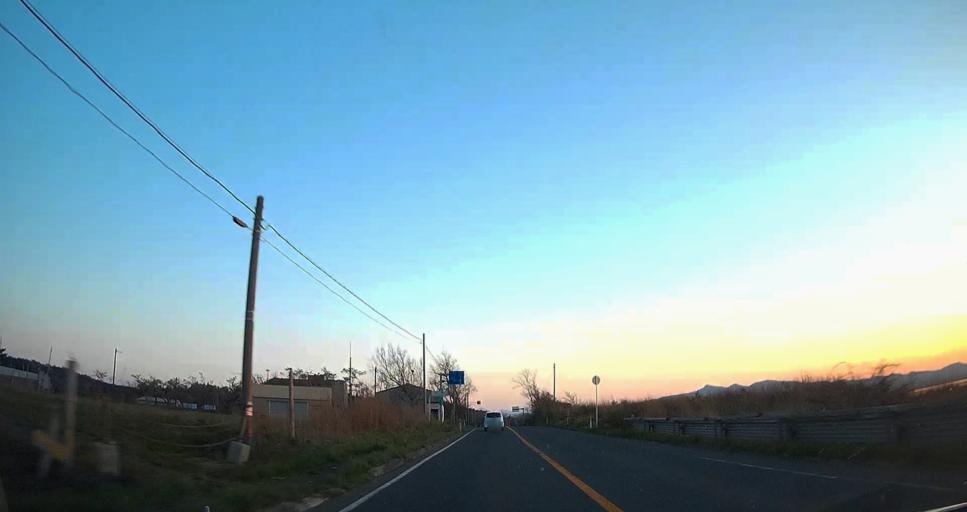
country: JP
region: Aomori
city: Misawa
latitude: 40.8874
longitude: 141.1609
